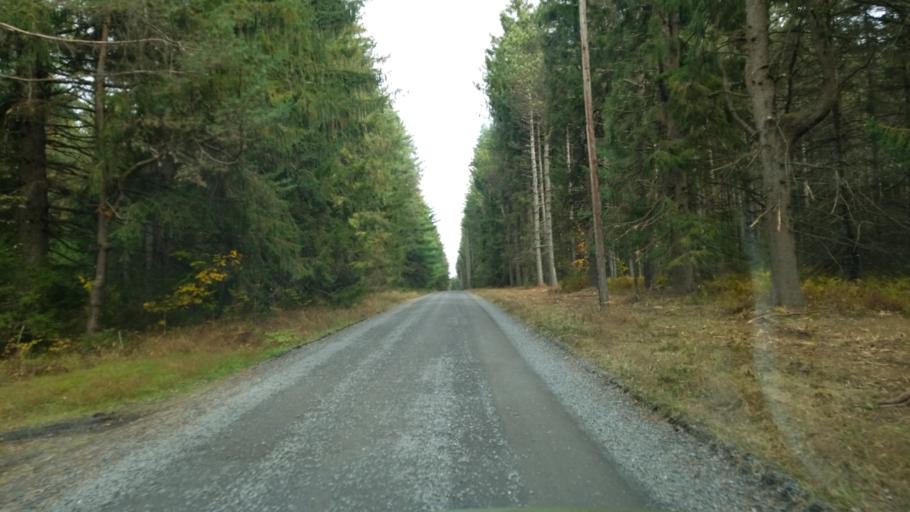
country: US
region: Pennsylvania
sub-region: Clearfield County
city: Clearfield
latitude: 41.1945
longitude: -78.4375
